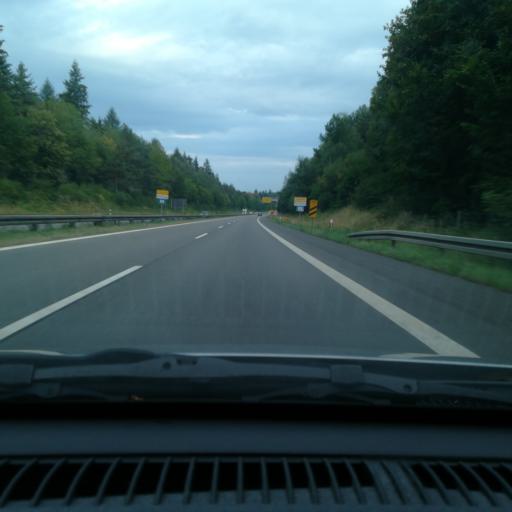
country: DE
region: Baden-Wuerttemberg
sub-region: Freiburg Region
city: Radolfzell am Bodensee
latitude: 47.7674
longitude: 8.9750
